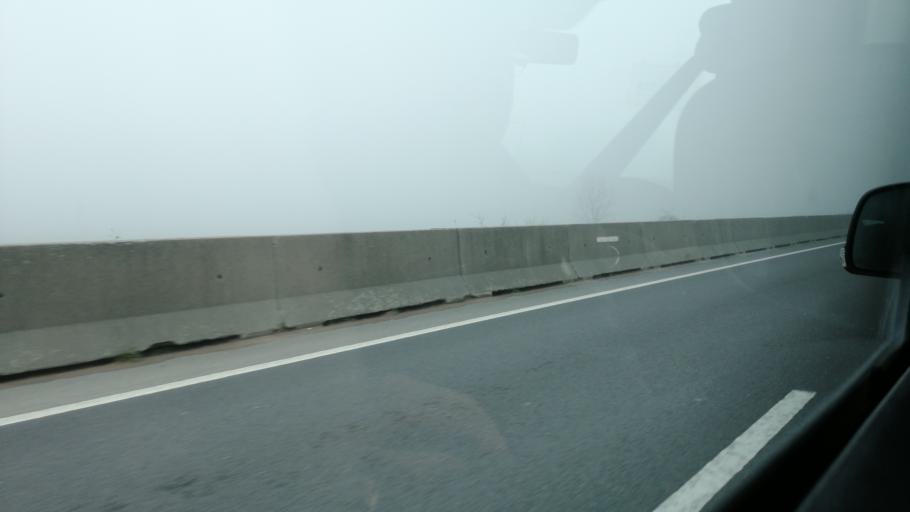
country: TR
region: Yalova
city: Taskopru
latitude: 40.6805
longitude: 29.3682
